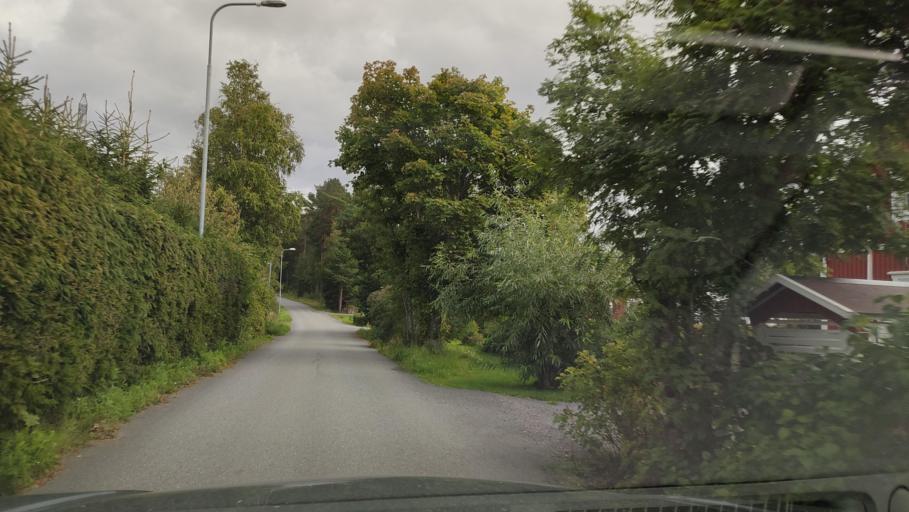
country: FI
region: Ostrobothnia
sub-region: Sydosterbotten
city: Kristinestad
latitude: 62.2782
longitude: 21.3435
